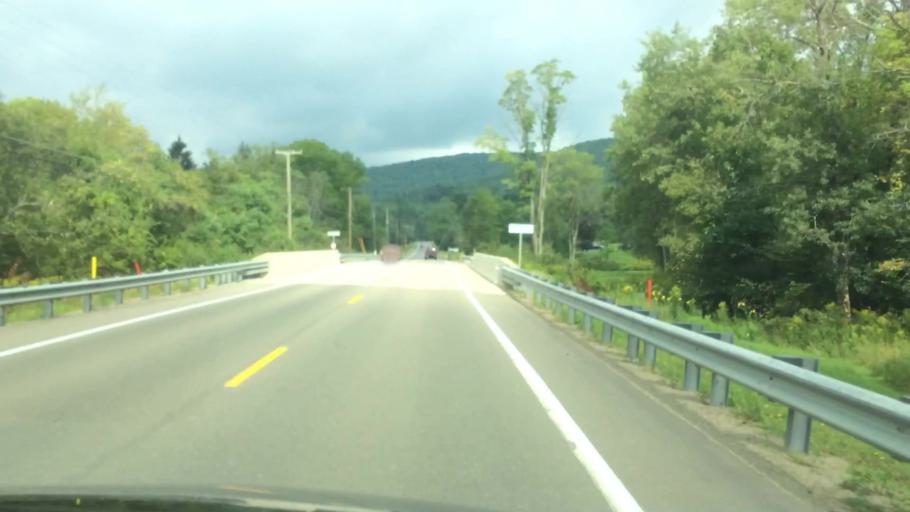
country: US
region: Pennsylvania
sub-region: McKean County
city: Bradford
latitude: 41.8977
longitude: -78.6090
